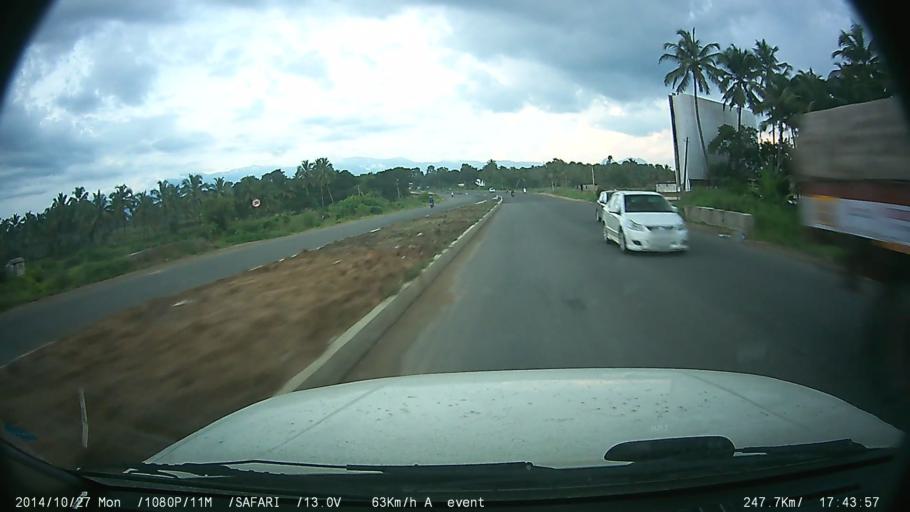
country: IN
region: Kerala
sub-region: Palakkad district
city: Palakkad
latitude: 10.7263
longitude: 76.6082
